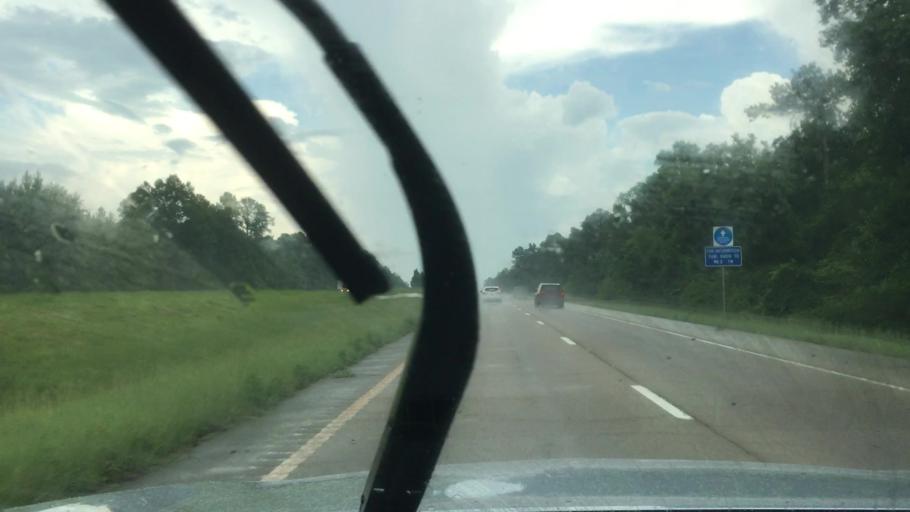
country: US
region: Mississippi
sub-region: Lamar County
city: Purvis
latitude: 31.1522
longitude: -89.3614
